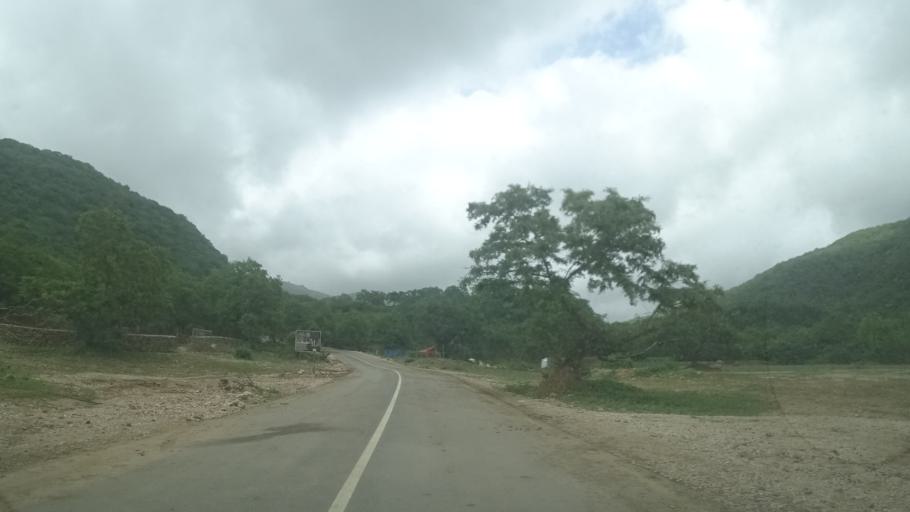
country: OM
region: Zufar
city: Salalah
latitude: 17.1048
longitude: 54.3554
